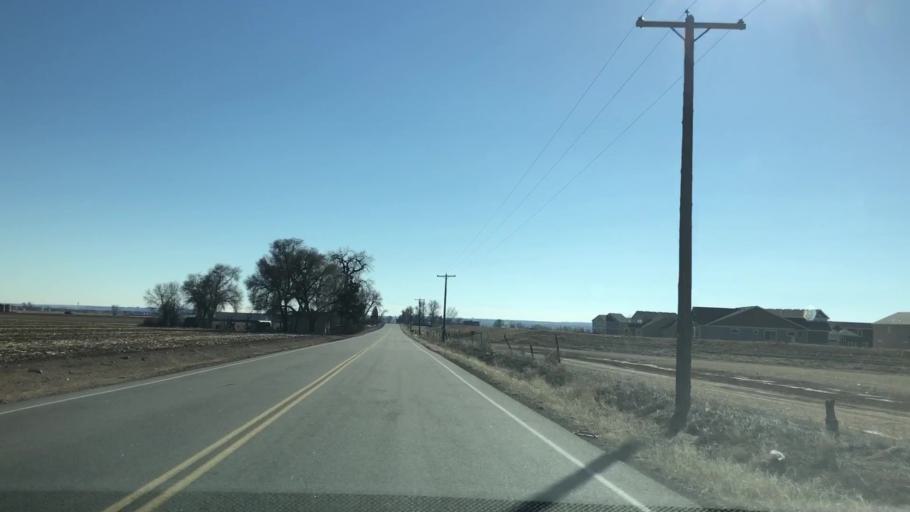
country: US
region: Colorado
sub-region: Weld County
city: Windsor
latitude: 40.5147
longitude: -104.9442
